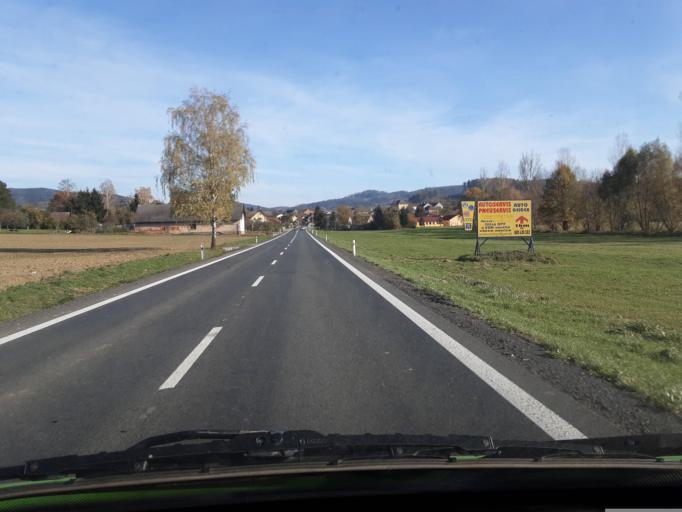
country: CZ
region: Plzensky
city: Klatovy
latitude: 49.3627
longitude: 13.3480
